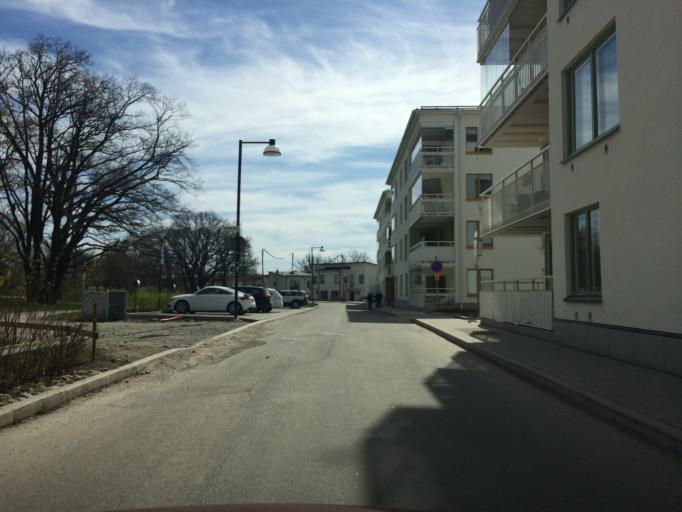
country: SE
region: Stockholm
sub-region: Huddinge Kommun
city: Huddinge
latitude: 59.2797
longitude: 17.9779
